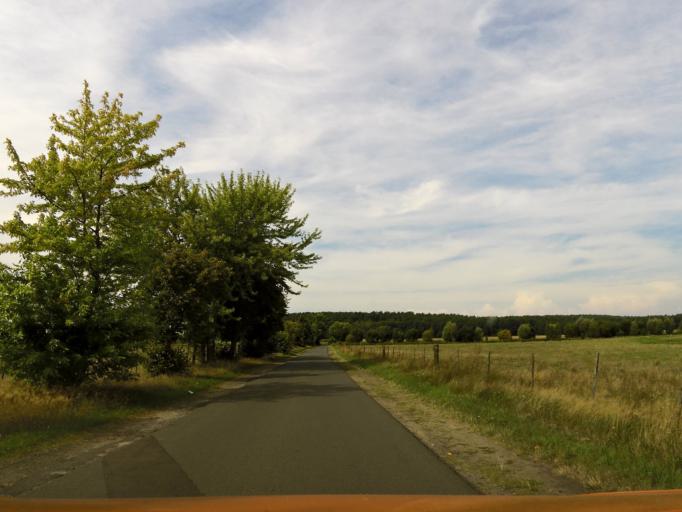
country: DE
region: Brandenburg
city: Michendorf
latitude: 52.2379
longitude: 13.1037
